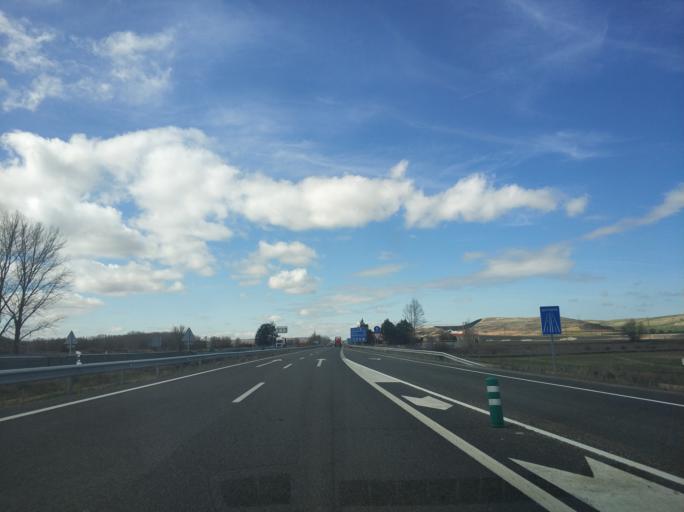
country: ES
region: Castille and Leon
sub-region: Provincia de Burgos
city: Frandovinez
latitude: 42.2992
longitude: -3.8366
